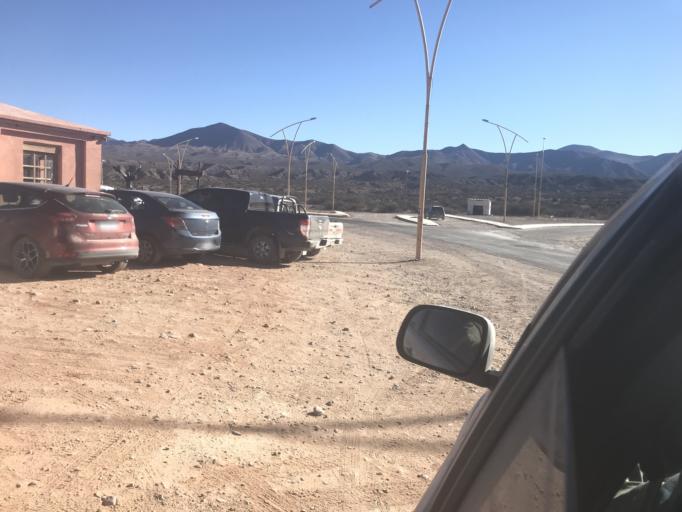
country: AR
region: Jujuy
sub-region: Departamento de Humahuaca
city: Humahuaca
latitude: -23.2159
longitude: -65.3529
